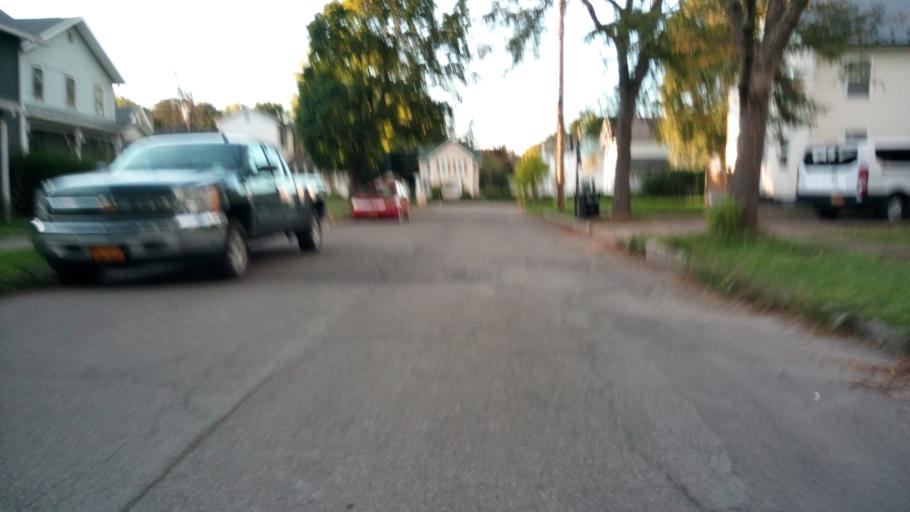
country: US
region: New York
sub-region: Chemung County
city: Elmira
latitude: 42.1006
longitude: -76.7995
